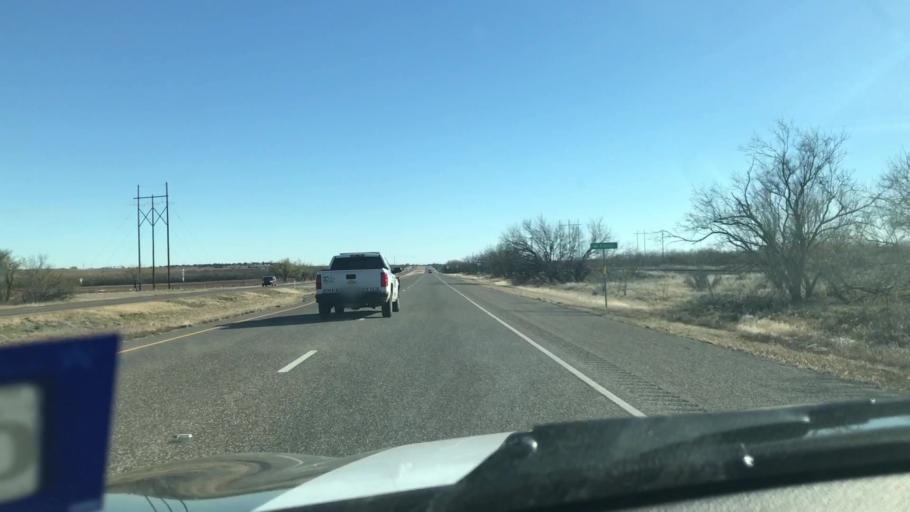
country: US
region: Texas
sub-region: Scurry County
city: Snyder
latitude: 32.8194
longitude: -100.9784
